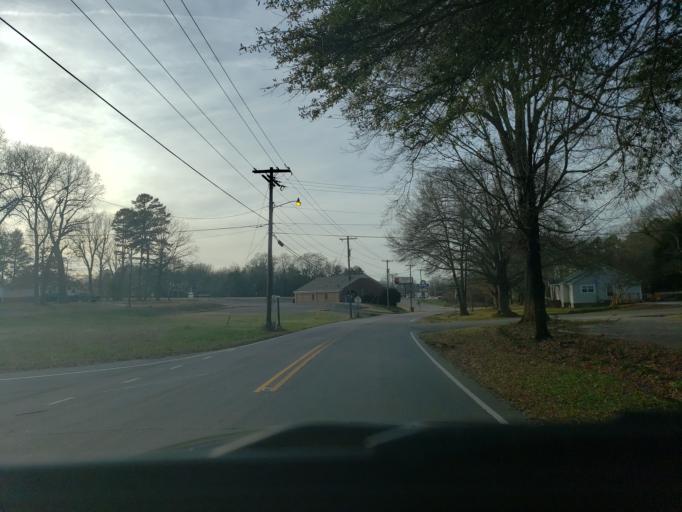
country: US
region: North Carolina
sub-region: Cleveland County
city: Shelby
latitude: 35.2895
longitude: -81.5616
